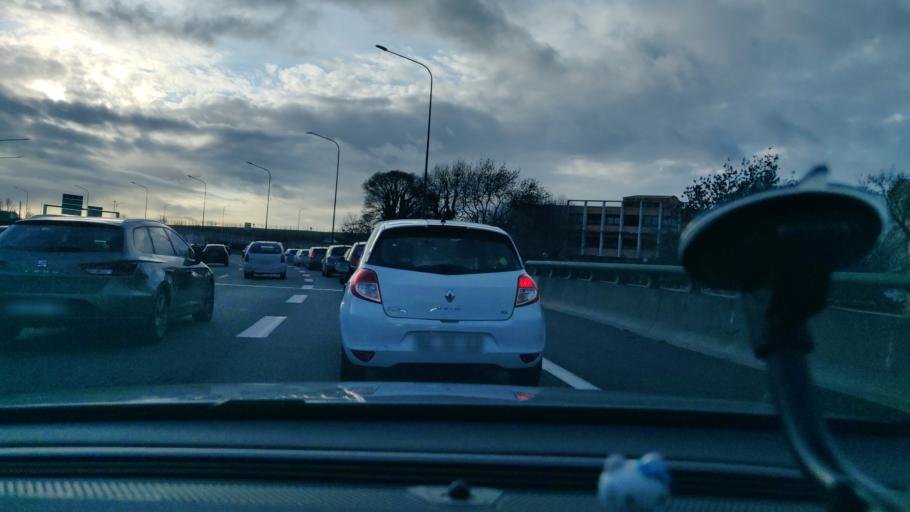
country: FR
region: Midi-Pyrenees
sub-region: Departement de la Haute-Garonne
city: Blagnac
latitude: 43.6159
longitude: 1.3896
